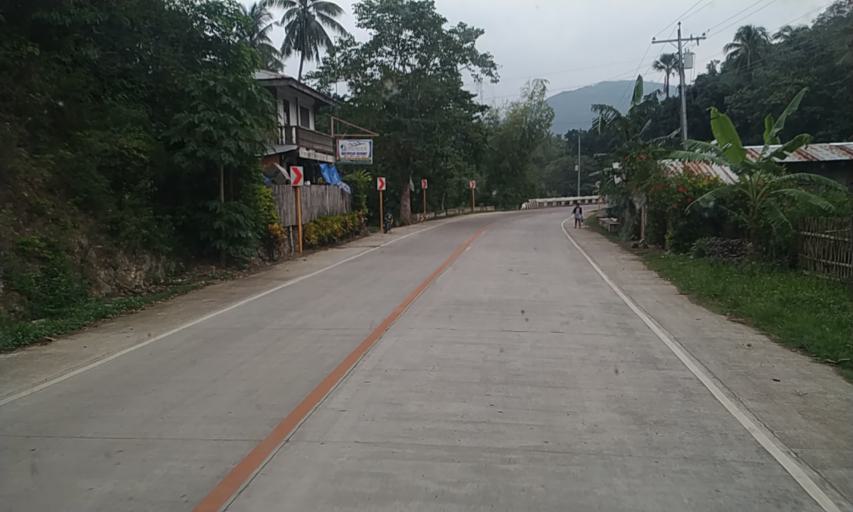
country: PH
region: Central Visayas
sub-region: Province of Negros Oriental
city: Calamba
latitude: 10.1957
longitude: 123.2945
